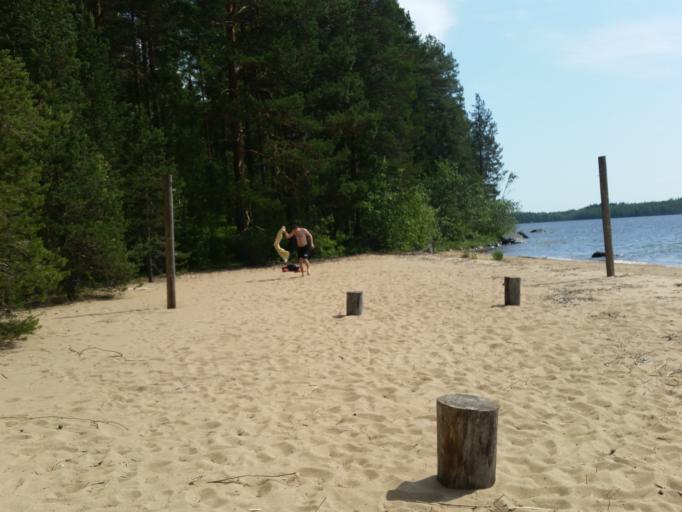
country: FI
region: Northern Savo
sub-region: Ylae-Savo
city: Keitele
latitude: 63.1029
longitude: 26.5291
